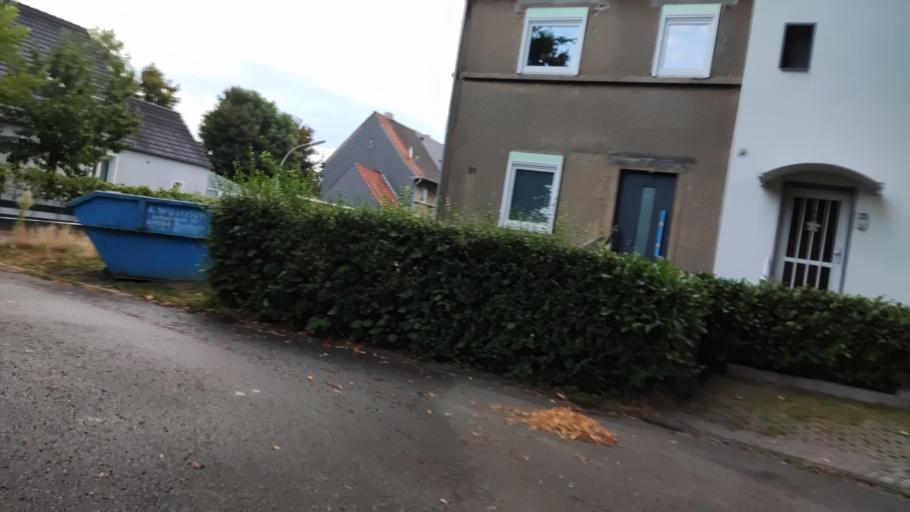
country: DE
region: North Rhine-Westphalia
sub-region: Regierungsbezirk Arnsberg
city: Herne
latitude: 51.5407
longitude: 7.2452
